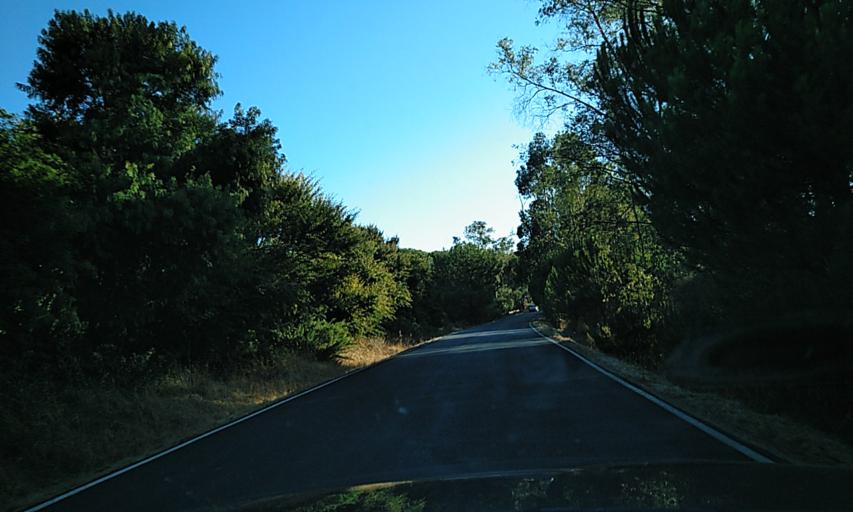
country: ES
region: Andalusia
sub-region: Provincia de Huelva
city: San Bartolome de la Torre
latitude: 37.3983
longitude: -7.1258
